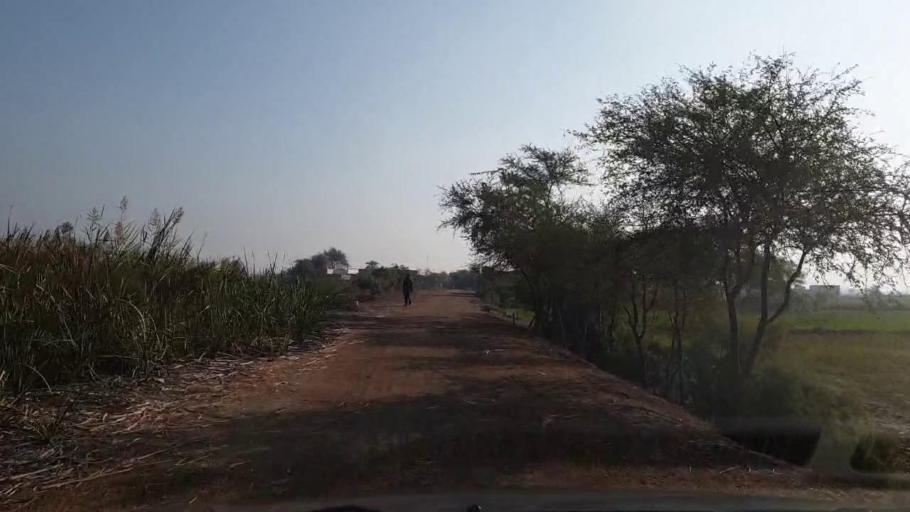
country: PK
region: Sindh
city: Sinjhoro
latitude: 26.0343
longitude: 68.7893
